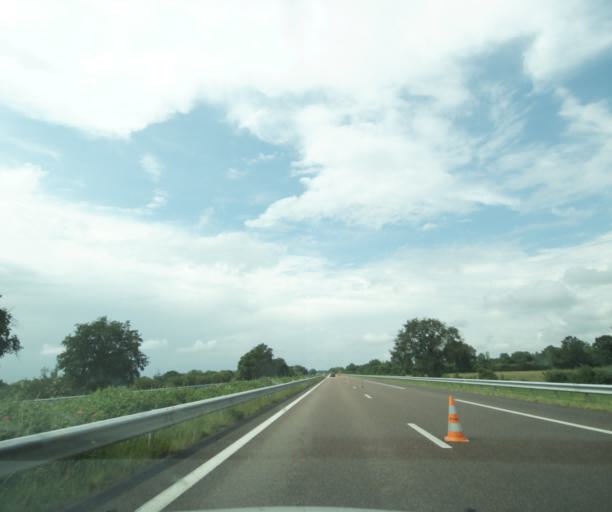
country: FR
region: Auvergne
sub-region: Departement de l'Allier
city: Estivareilles
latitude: 46.4595
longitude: 2.6837
